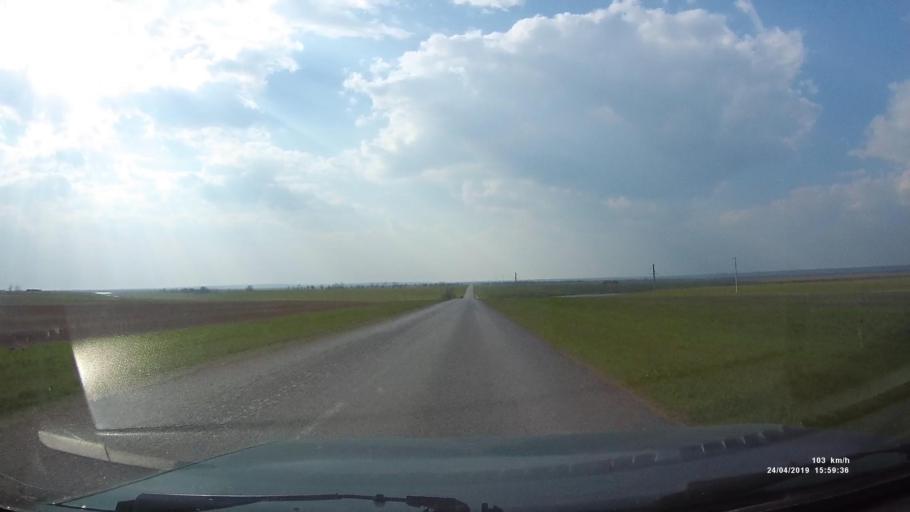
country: RU
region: Rostov
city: Sovetskoye
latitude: 46.6249
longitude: 42.4691
